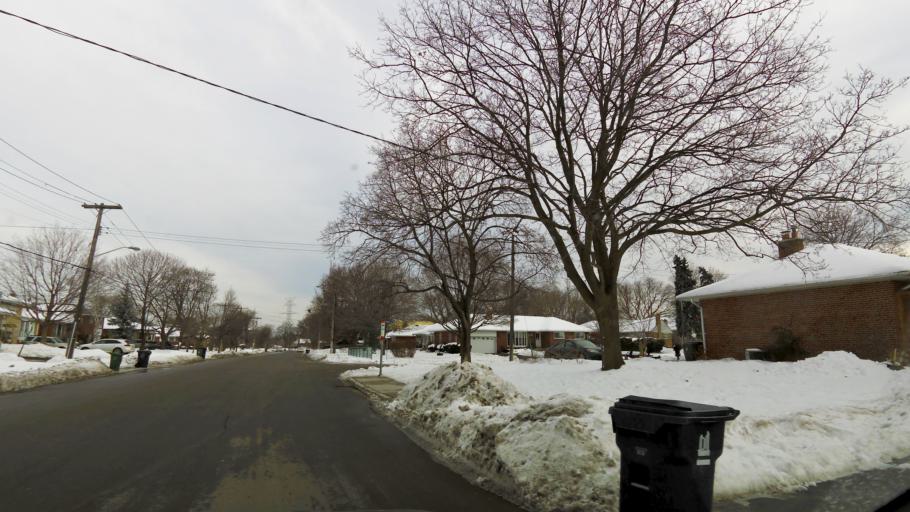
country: CA
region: Ontario
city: Etobicoke
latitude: 43.6665
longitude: -79.5584
